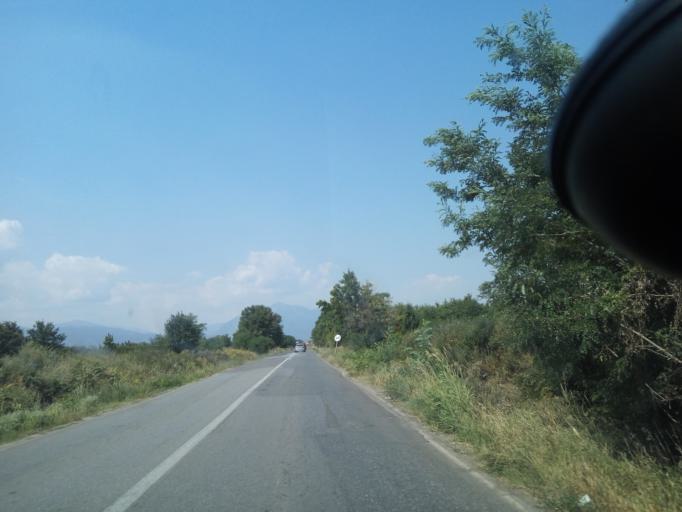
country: XK
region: Gjakova
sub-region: Komuna e Decanit
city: Gllogjan
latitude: 42.4388
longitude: 20.3694
